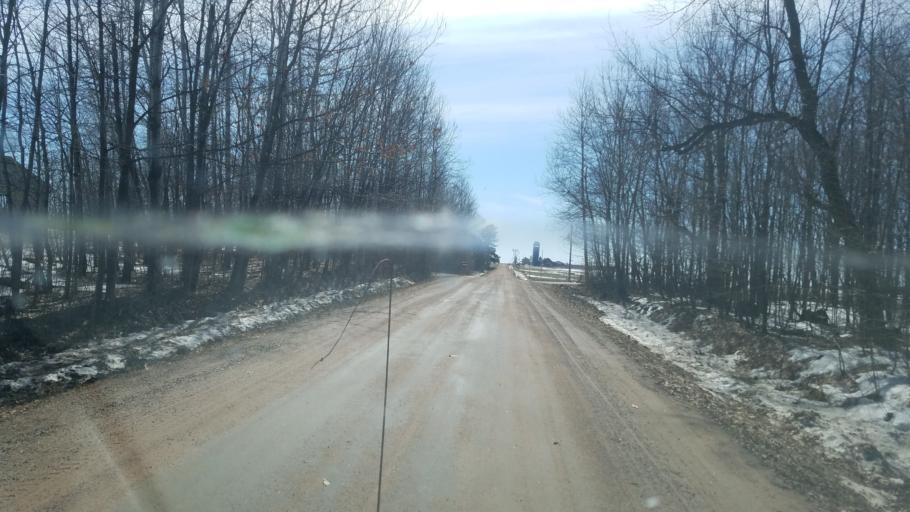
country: US
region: Wisconsin
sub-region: Clark County
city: Loyal
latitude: 44.6230
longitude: -90.4271
